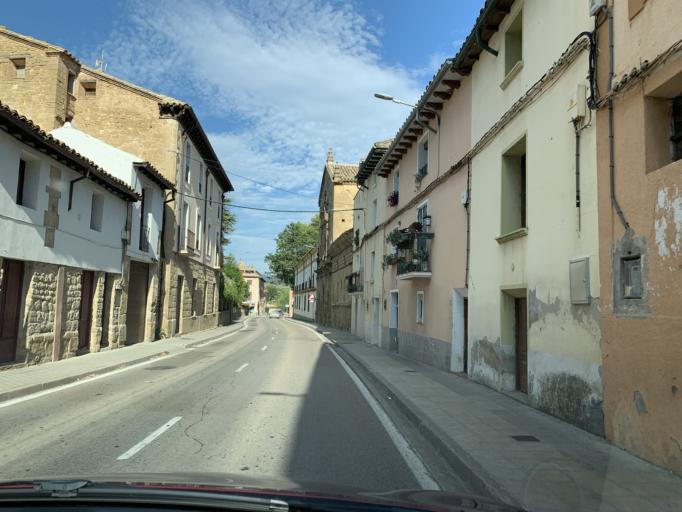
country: ES
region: Aragon
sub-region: Provincia de Huesca
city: Ayerbe
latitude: 42.2749
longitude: -0.6886
